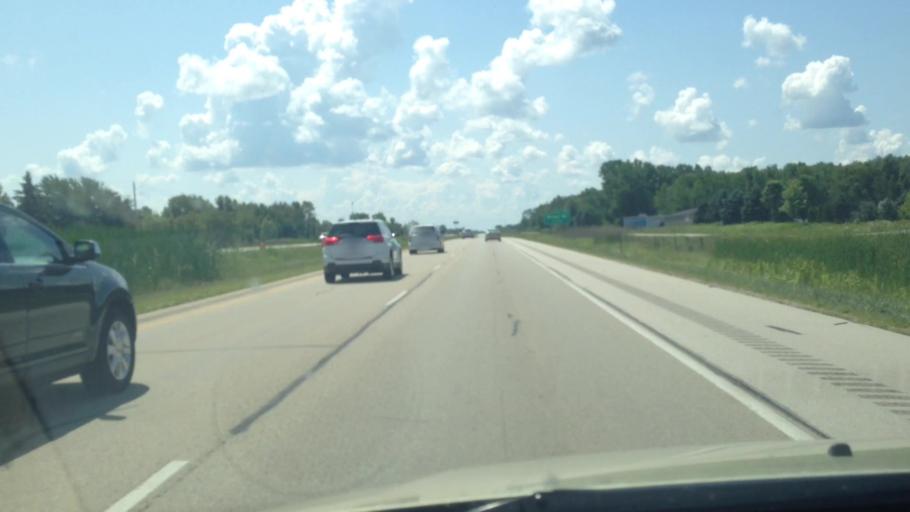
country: US
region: Wisconsin
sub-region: Brown County
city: Suamico
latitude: 44.6982
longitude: -88.0508
